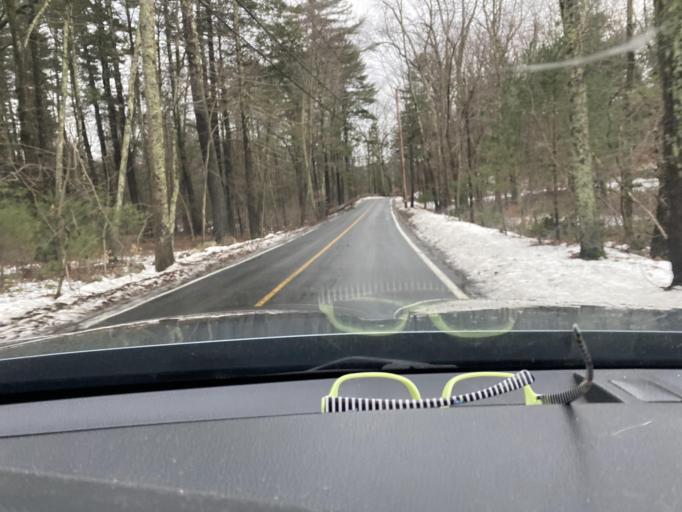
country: US
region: Massachusetts
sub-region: Middlesex County
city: Sherborn
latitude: 42.2130
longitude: -71.3802
